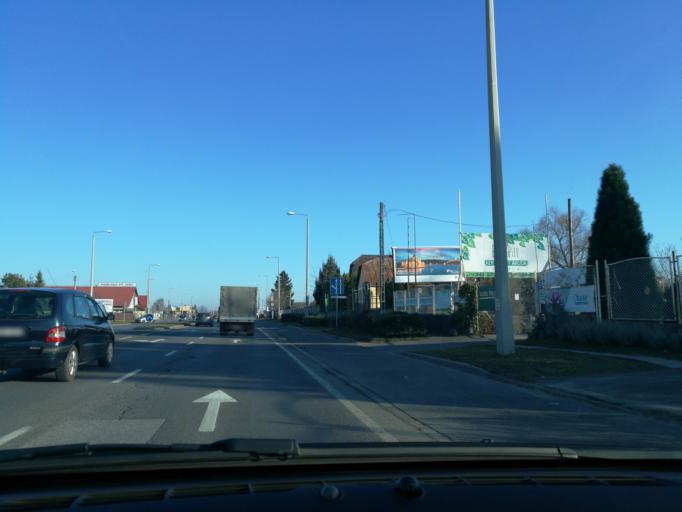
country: HU
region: Szabolcs-Szatmar-Bereg
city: Nyiregyhaza
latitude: 47.9509
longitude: 21.7627
